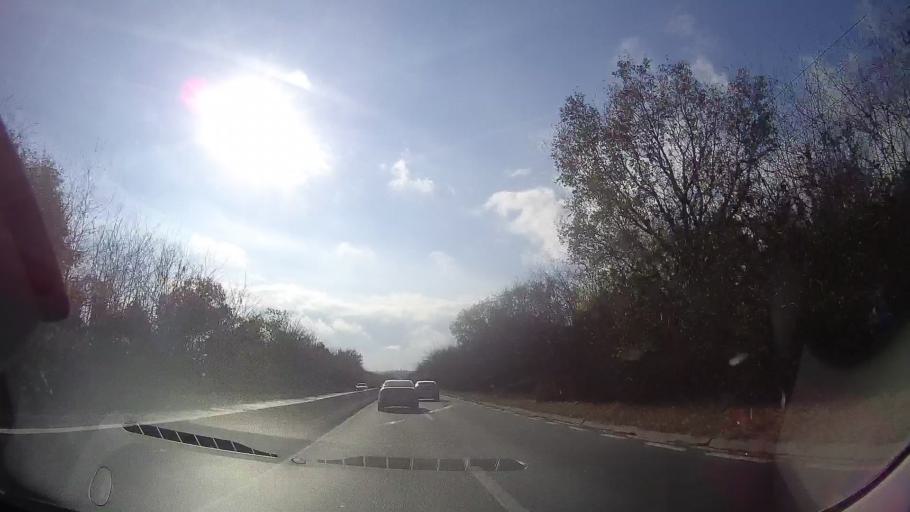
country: RO
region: Constanta
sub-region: Comuna Agigea
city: Agigea
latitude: 44.1246
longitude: 28.6141
